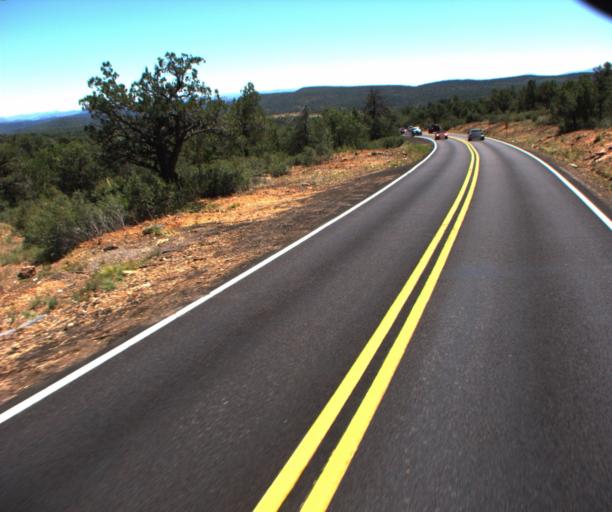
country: US
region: Arizona
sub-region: Gila County
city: Pine
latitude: 34.3441
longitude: -111.4261
